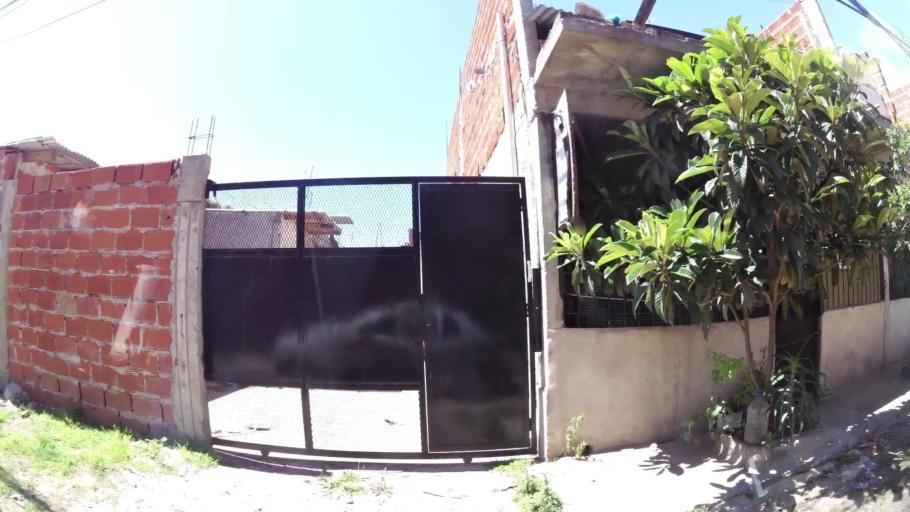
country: AR
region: Buenos Aires
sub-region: Partido de Quilmes
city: Quilmes
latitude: -34.7260
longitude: -58.3156
